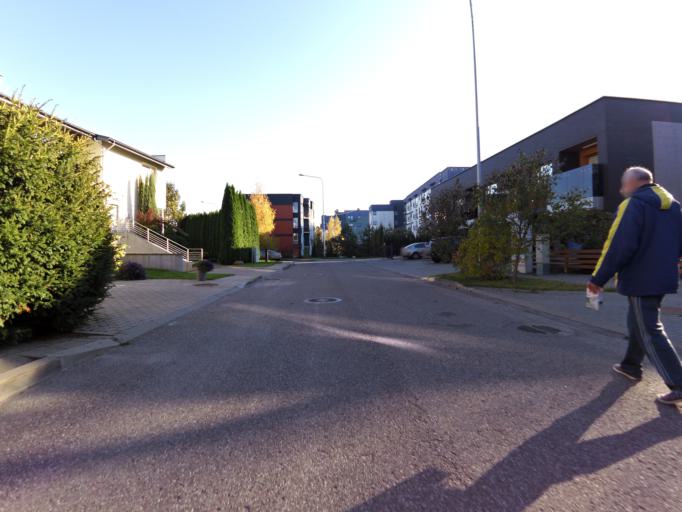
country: LT
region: Vilnius County
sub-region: Vilnius
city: Fabijoniskes
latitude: 54.7371
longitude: 25.2755
